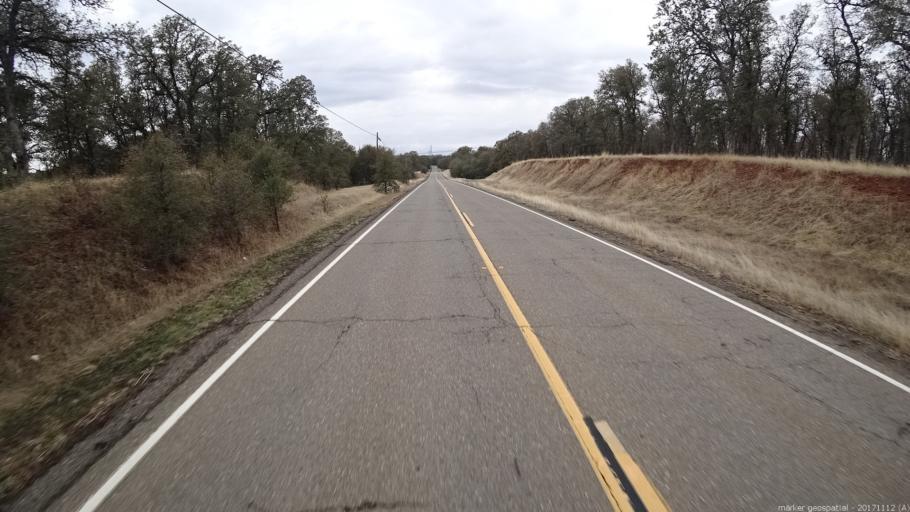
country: US
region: California
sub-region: Shasta County
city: Palo Cedro
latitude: 40.4766
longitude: -122.1967
